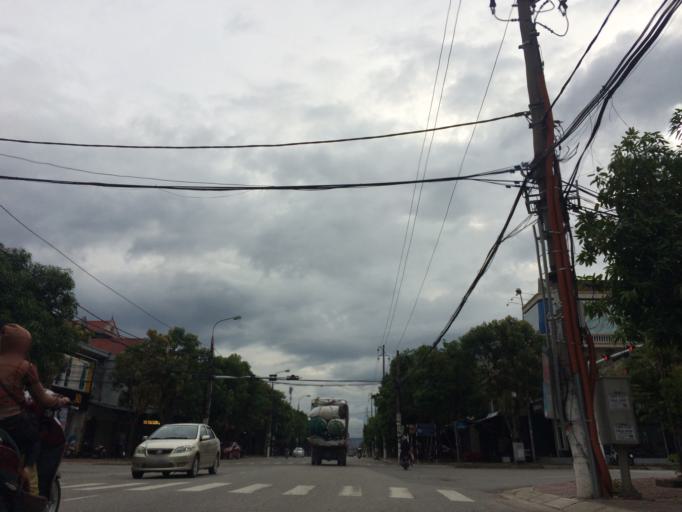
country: VN
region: Ha Tinh
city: Ha Tinh
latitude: 18.3482
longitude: 105.8959
